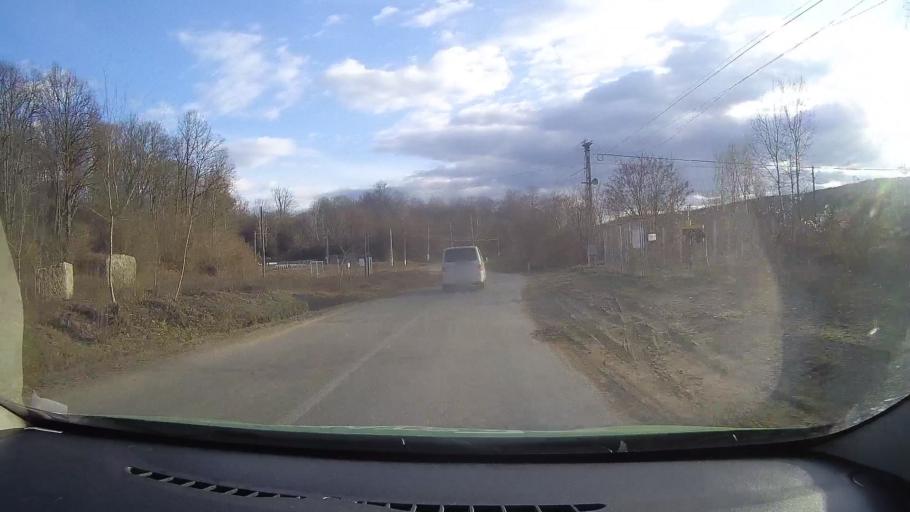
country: RO
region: Dambovita
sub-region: Comuna Ocnita
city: Ocnita
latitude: 44.9681
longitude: 25.5483
